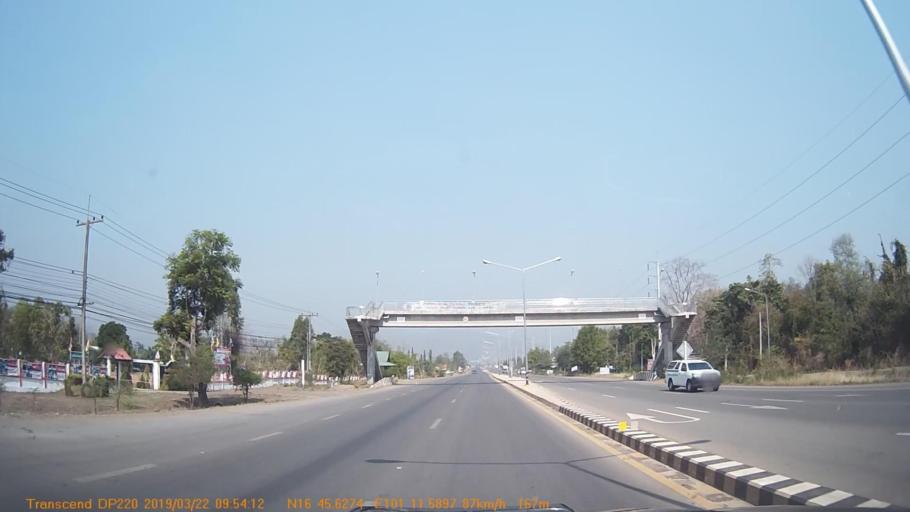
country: TH
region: Phetchabun
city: Lom Sak
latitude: 16.7608
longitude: 101.1926
